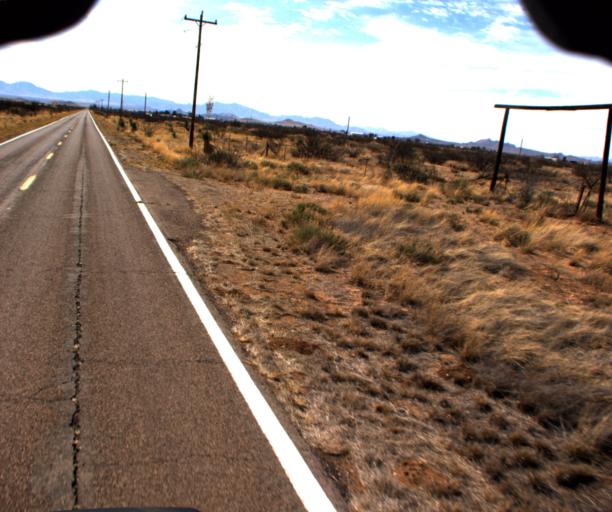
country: US
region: Arizona
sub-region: Cochise County
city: Willcox
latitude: 31.8762
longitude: -109.6014
